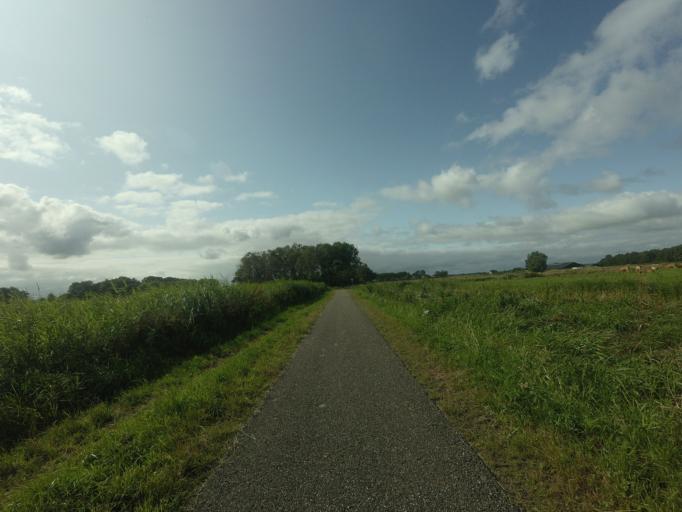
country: NL
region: North Holland
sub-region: Gemeente Haarlem
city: Haarlem
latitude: 52.3989
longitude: 4.6985
